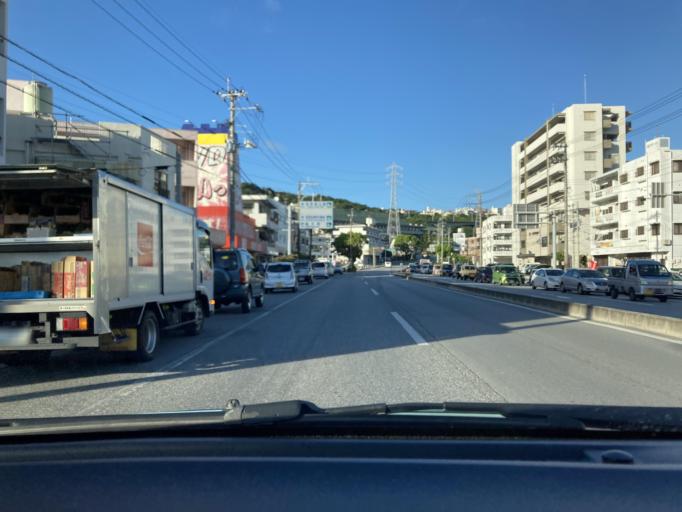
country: JP
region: Okinawa
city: Tomigusuku
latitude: 26.1989
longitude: 127.7138
